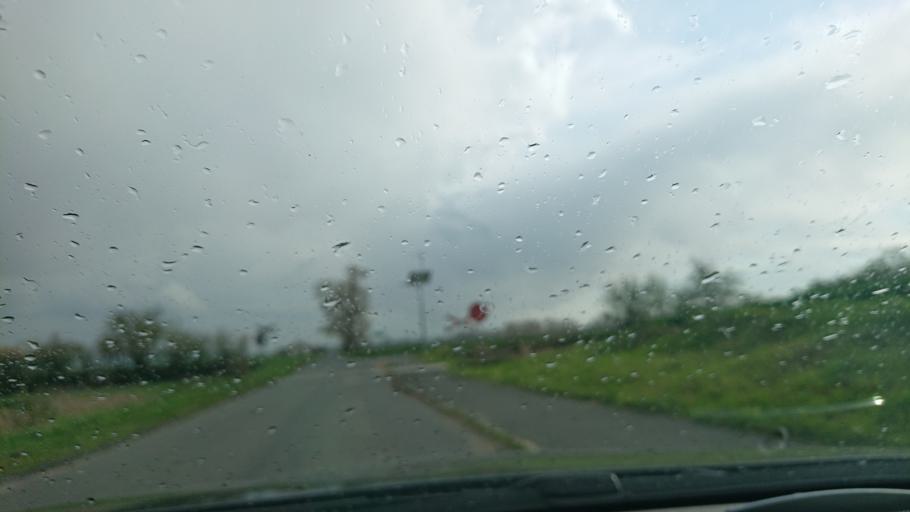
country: PL
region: Greater Poland Voivodeship
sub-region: Powiat gnieznienski
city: Klecko
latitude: 52.5866
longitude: 17.4851
